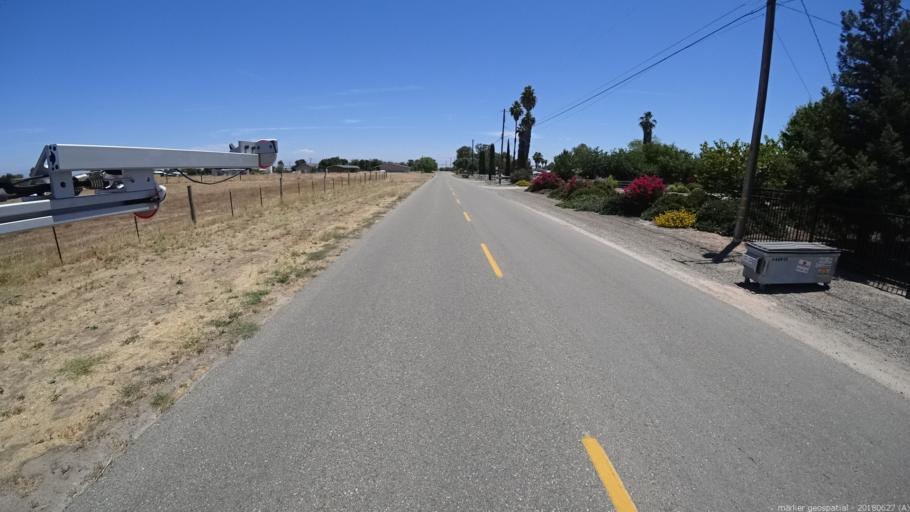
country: US
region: California
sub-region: Madera County
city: Bonadelle Ranchos-Madera Ranchos
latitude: 36.9448
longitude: -119.8981
